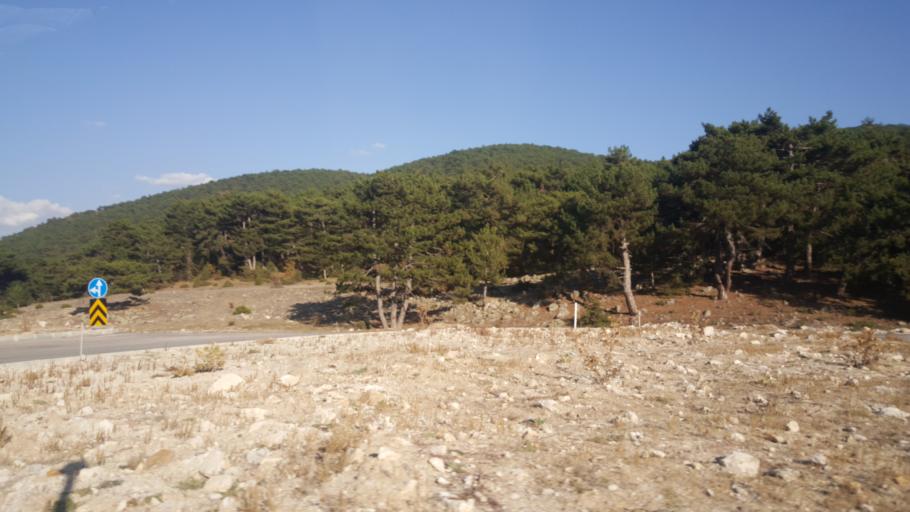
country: TR
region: Afyonkarahisar
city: Ihsaniye
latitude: 39.0971
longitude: 30.5758
